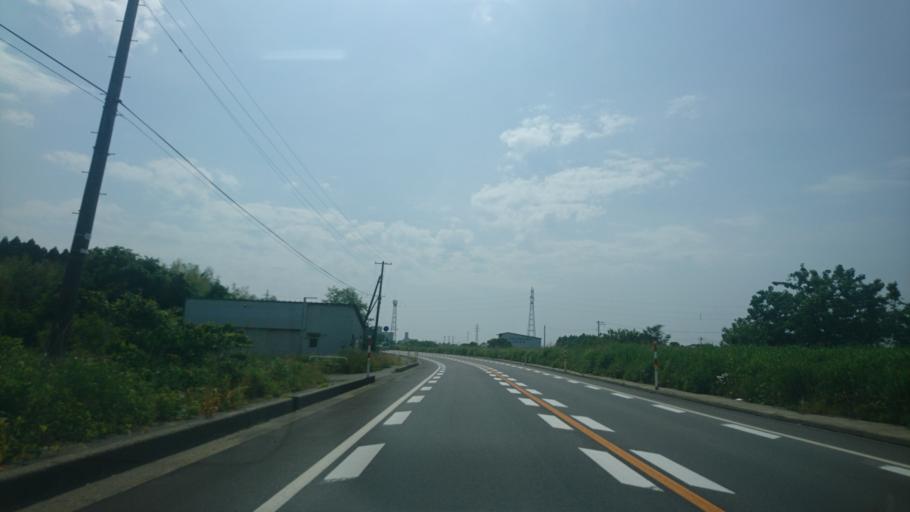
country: JP
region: Niigata
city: Shibata
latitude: 38.0618
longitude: 139.4192
